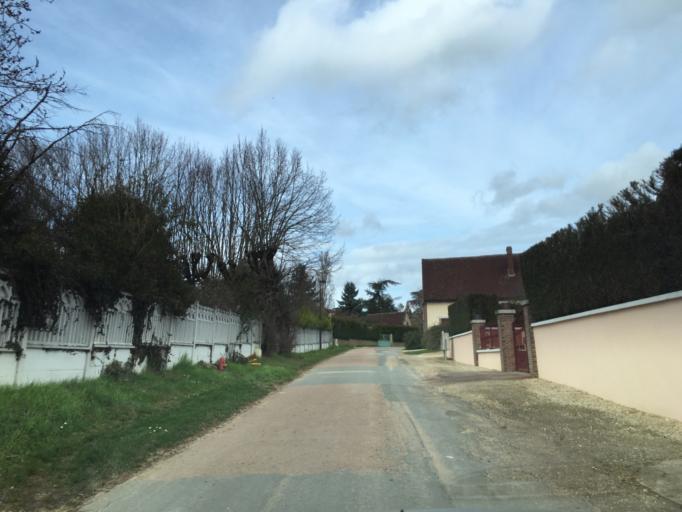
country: FR
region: Bourgogne
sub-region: Departement de l'Yonne
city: Fleury-la-Vallee
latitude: 47.8604
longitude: 3.4079
